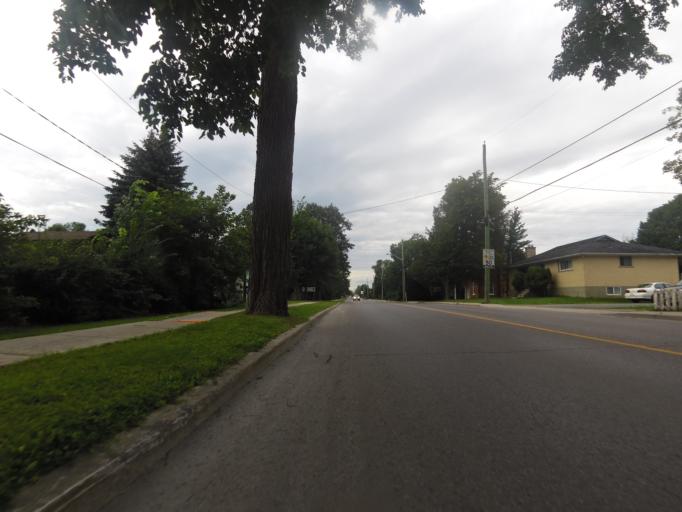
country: CA
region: Ontario
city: Carleton Place
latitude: 45.1320
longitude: -76.1316
